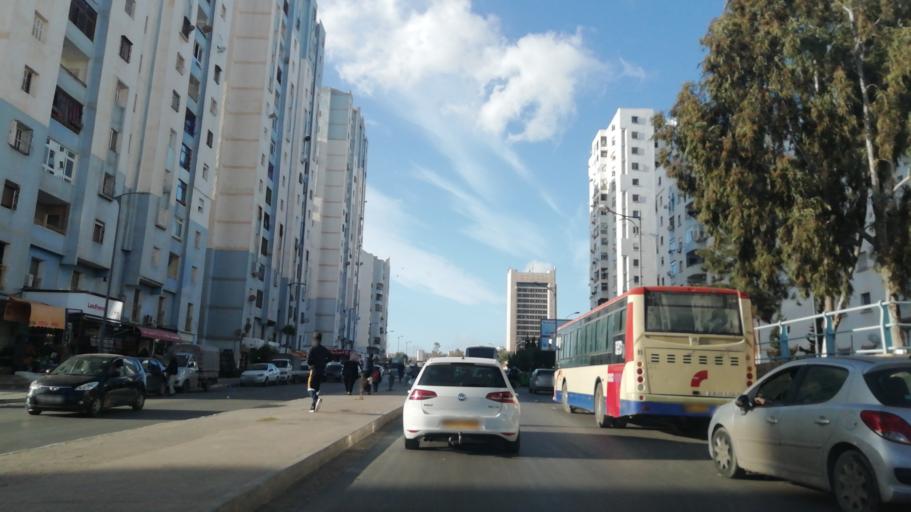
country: DZ
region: Oran
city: Bir el Djir
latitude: 35.7009
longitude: -0.5753
